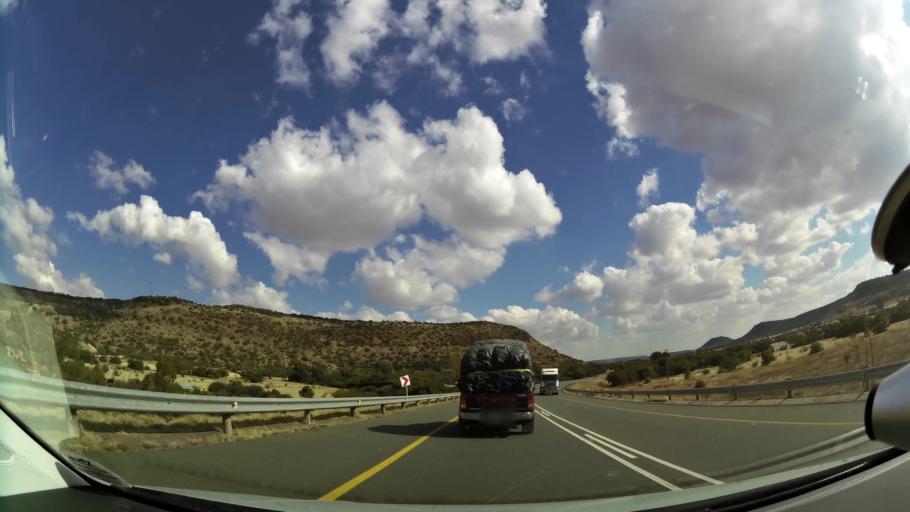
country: ZA
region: Orange Free State
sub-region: Mangaung Metropolitan Municipality
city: Bloemfontein
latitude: -29.1584
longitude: 26.0539
